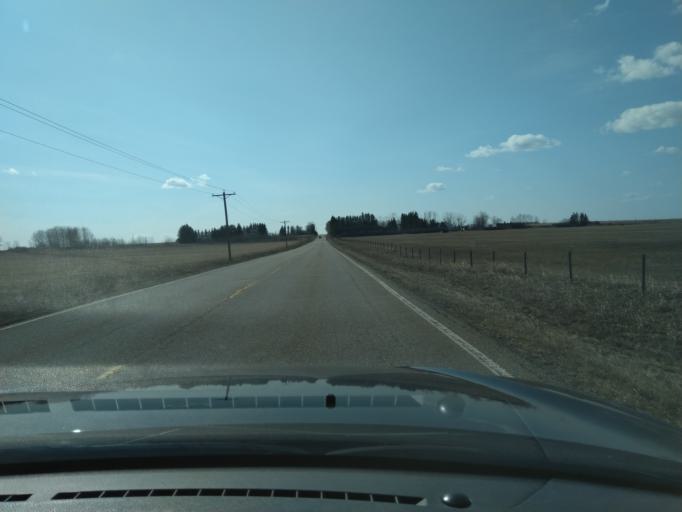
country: CA
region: Alberta
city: Cochrane
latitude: 51.0961
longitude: -114.3316
